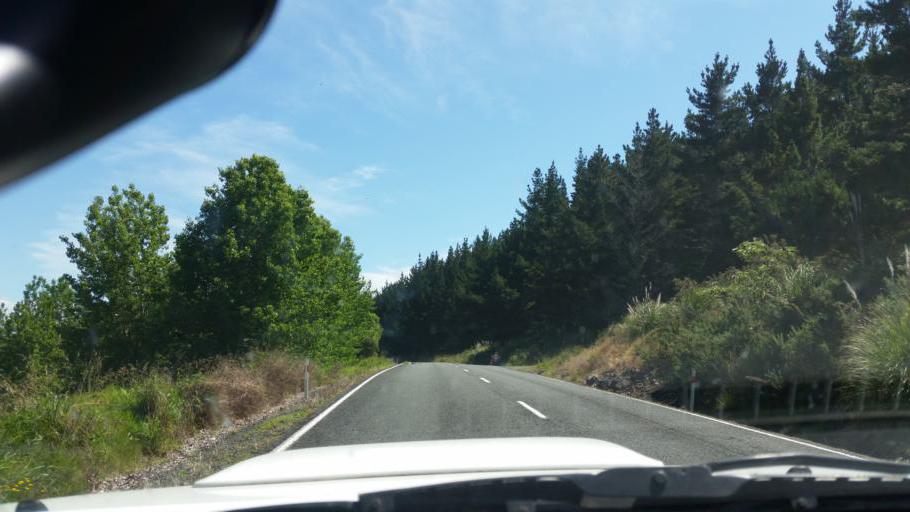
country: NZ
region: Auckland
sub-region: Auckland
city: Wellsford
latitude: -36.2068
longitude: 174.3932
